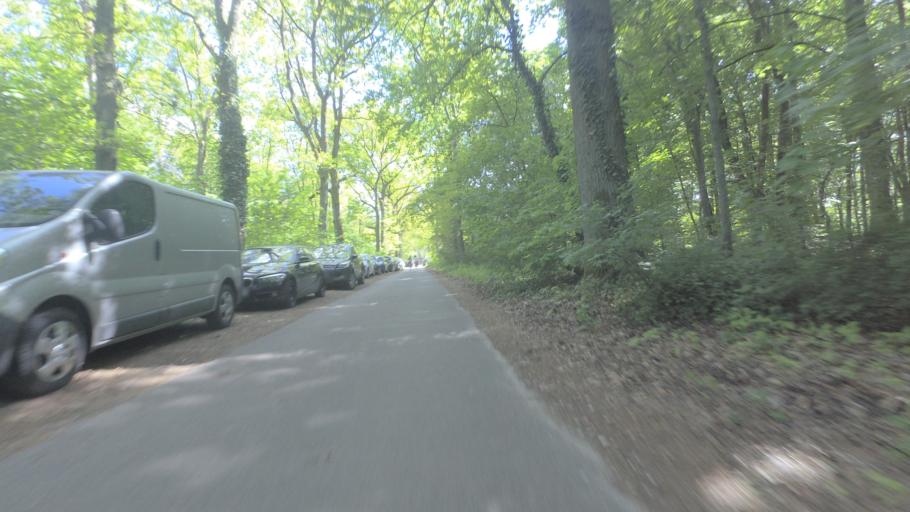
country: DE
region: Brandenburg
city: Woltersdorf
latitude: 52.4366
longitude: 13.7678
